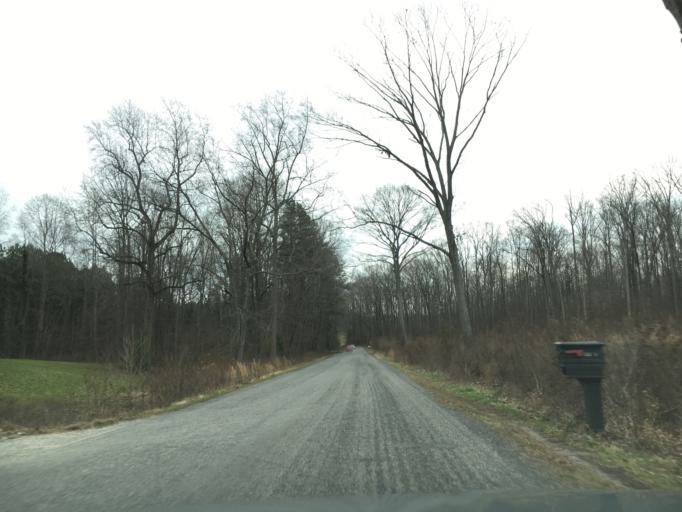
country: US
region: Virginia
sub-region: Amelia County
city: Amelia Court House
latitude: 37.4182
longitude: -77.9872
